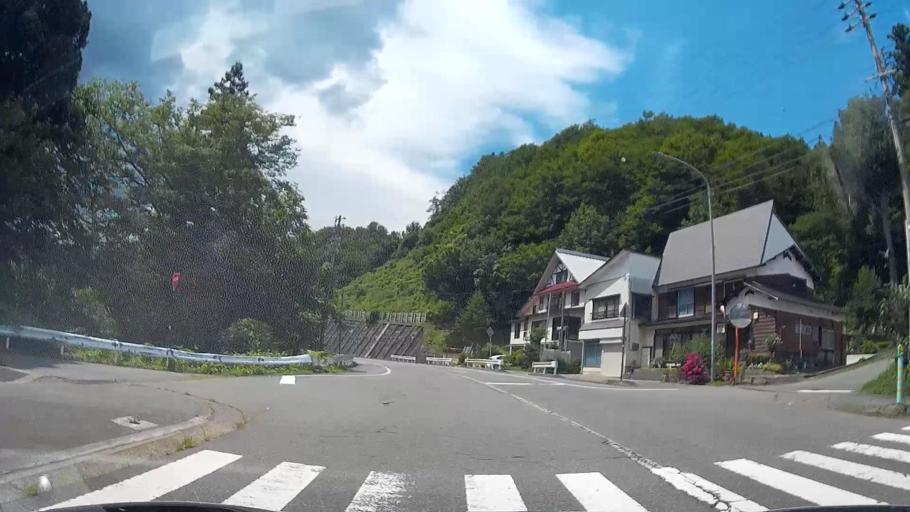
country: JP
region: Niigata
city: Tokamachi
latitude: 36.9908
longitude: 138.5739
